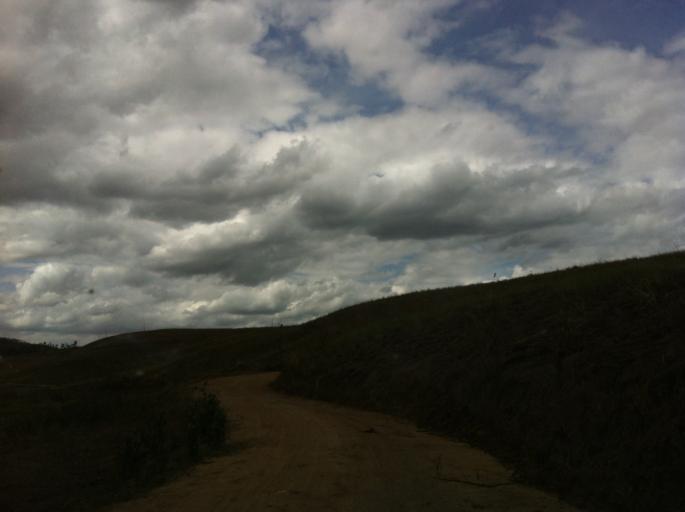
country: BR
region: Alagoas
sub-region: Ibateguara
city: Ibateguara
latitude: -8.9616
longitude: -35.9512
